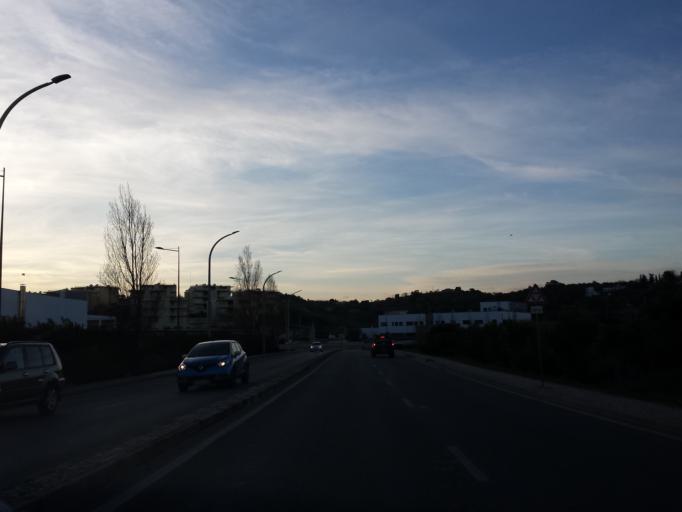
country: PT
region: Faro
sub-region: Lagos
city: Lagos
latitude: 37.1139
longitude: -8.6790
